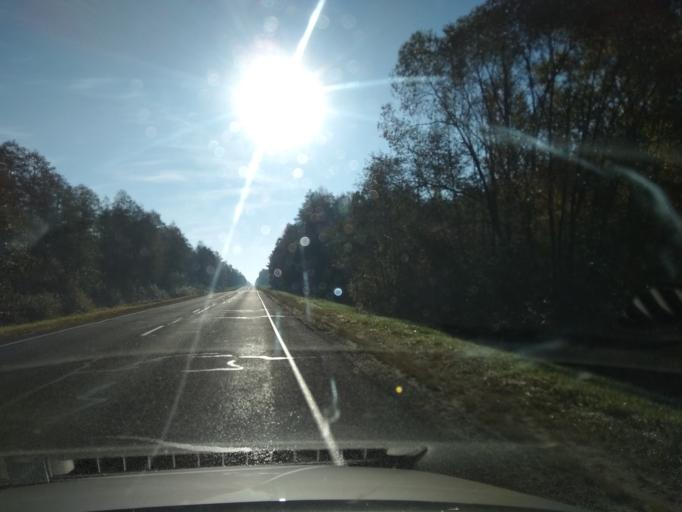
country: BY
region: Brest
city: Malaryta
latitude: 51.8895
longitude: 24.1449
